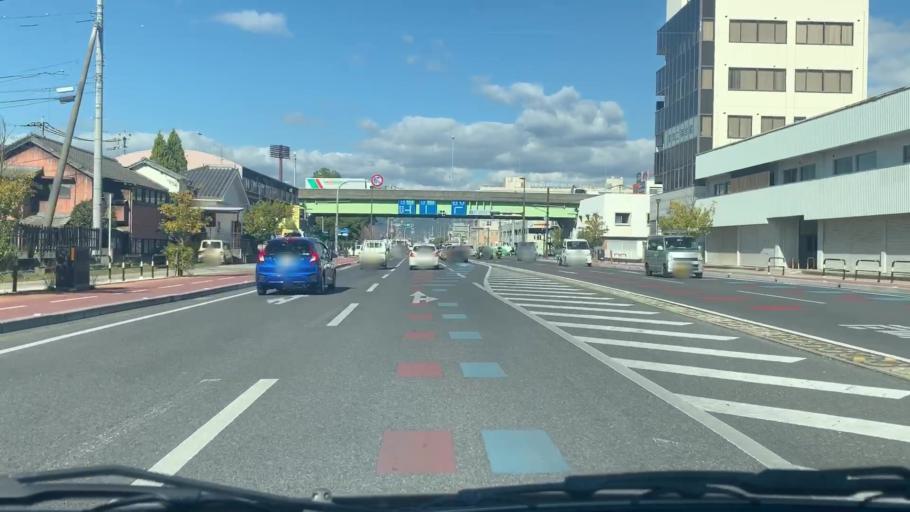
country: JP
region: Saga Prefecture
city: Saga-shi
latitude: 33.2733
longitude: 130.2940
